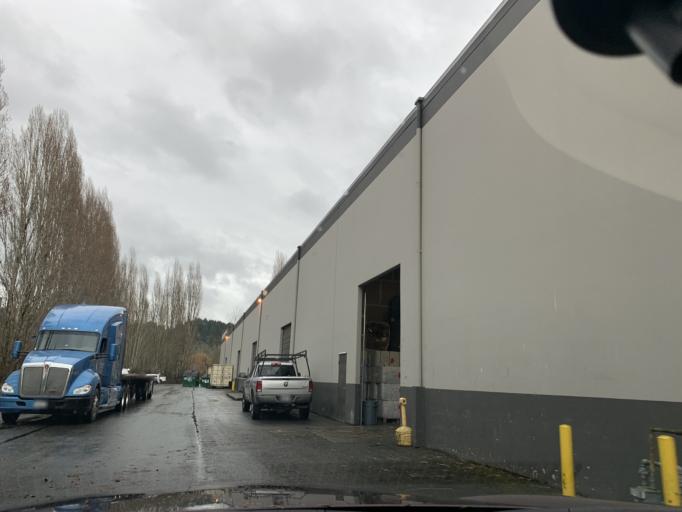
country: US
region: Washington
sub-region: King County
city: Woodinville
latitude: 47.7418
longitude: -122.1560
